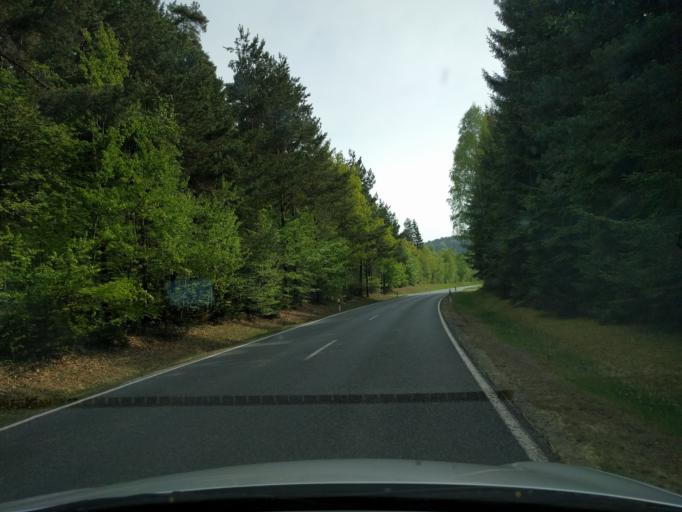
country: DE
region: Bavaria
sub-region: Upper Palatinate
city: Michelsneukirchen
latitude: 49.1445
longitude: 12.5612
